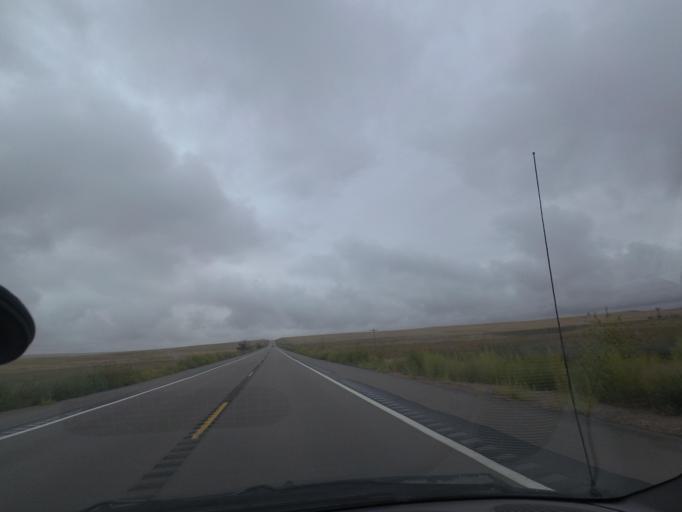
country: US
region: Colorado
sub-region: Lincoln County
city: Limon
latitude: 39.7400
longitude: -103.6843
